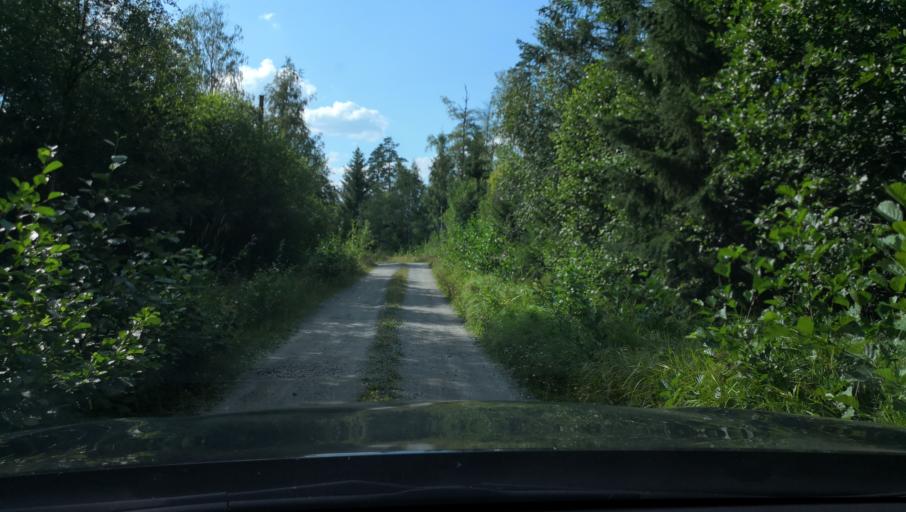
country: SE
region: Vaestmanland
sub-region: Vasteras
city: Skultuna
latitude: 59.7262
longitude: 16.3702
